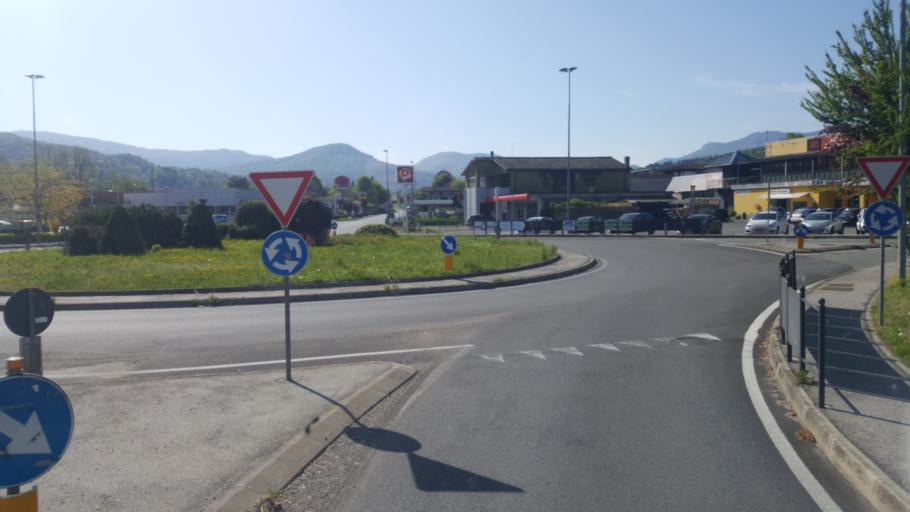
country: IT
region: Lombardy
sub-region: Provincia di Varese
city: Mesenzana
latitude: 45.9575
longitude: 8.7607
